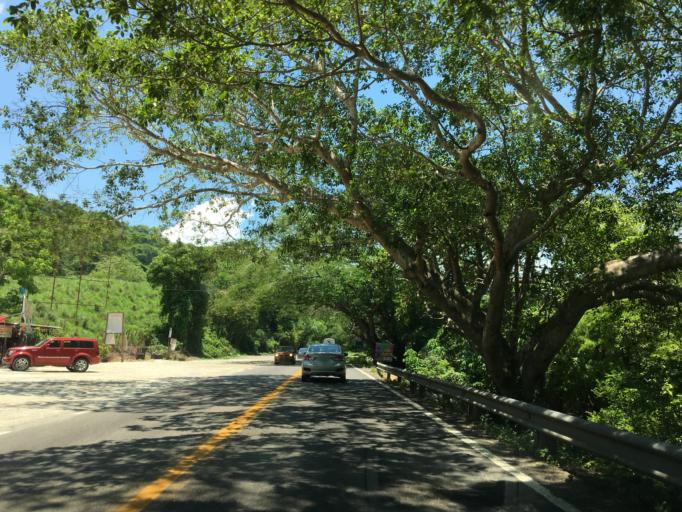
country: MX
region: Nayarit
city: Bucerias
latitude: 20.8314
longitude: -105.4053
